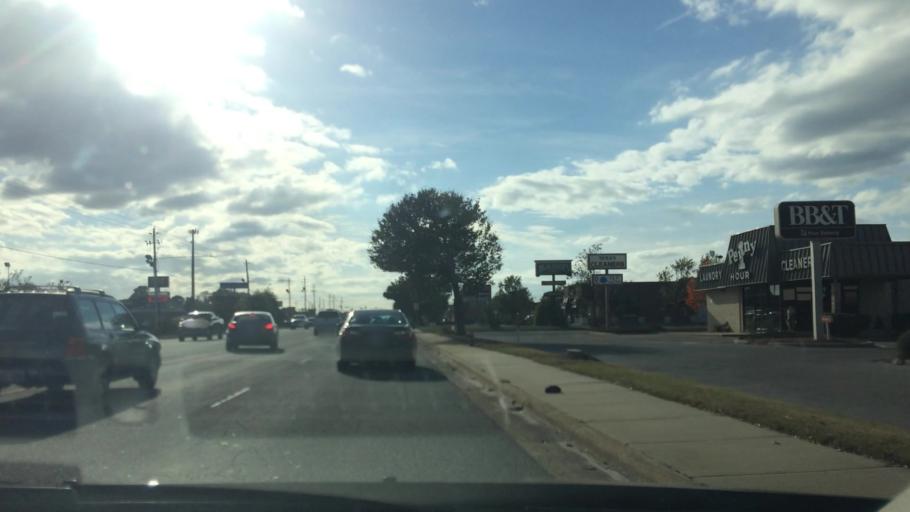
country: US
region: North Carolina
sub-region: Wayne County
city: Goldsboro
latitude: 35.3744
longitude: -77.9459
